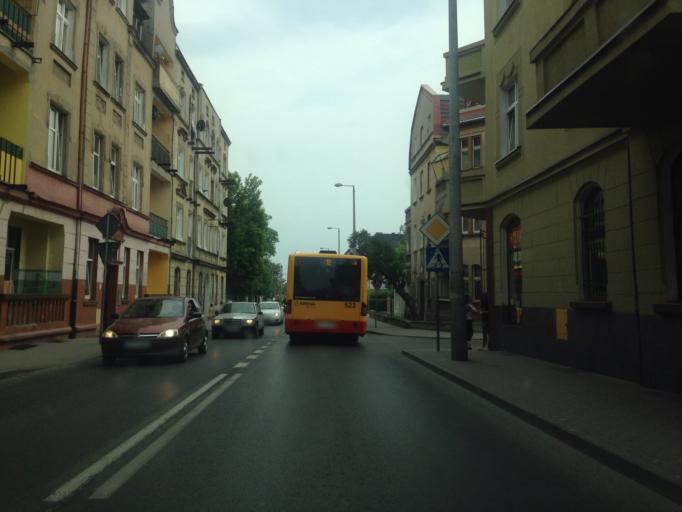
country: PL
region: Kujawsko-Pomorskie
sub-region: Grudziadz
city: Grudziadz
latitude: 53.5006
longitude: 18.7764
